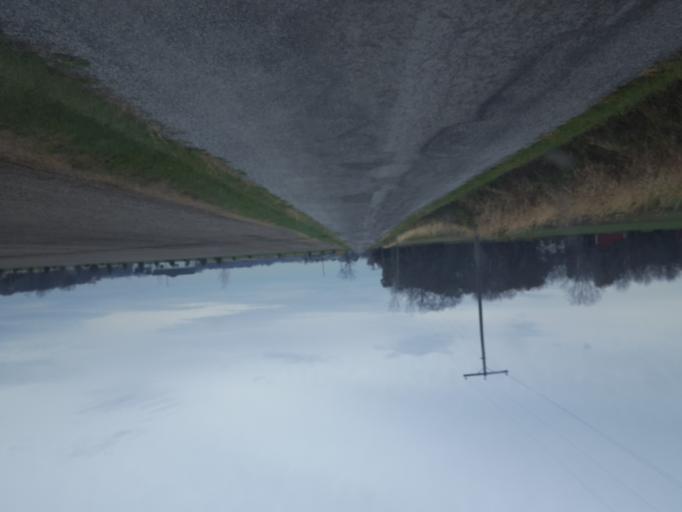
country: US
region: Ohio
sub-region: Delaware County
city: Ashley
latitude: 40.4526
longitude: -82.9222
